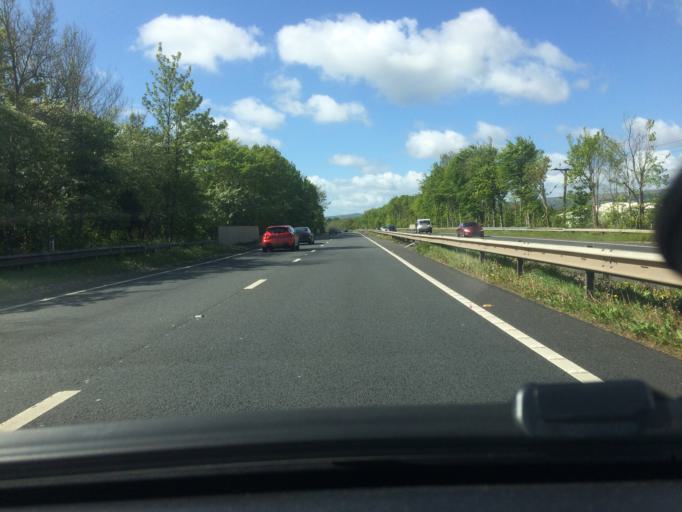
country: GB
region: Wales
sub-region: Wrexham
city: Wrexham
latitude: 53.0633
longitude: -3.0021
